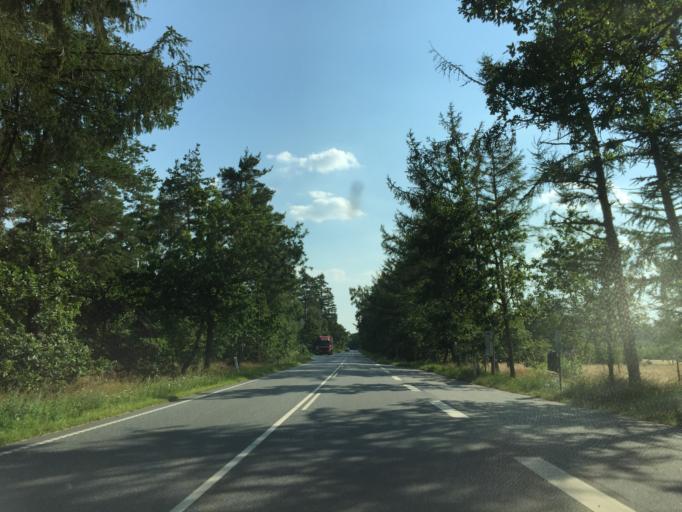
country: DK
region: Central Jutland
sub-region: Viborg Kommune
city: Bjerringbro
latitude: 56.3059
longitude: 9.6859
